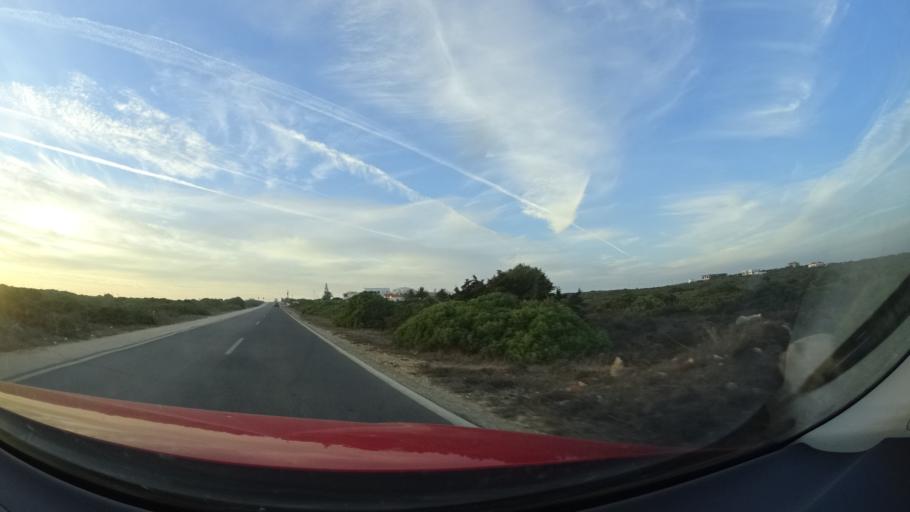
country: PT
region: Faro
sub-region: Vila do Bispo
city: Sagres
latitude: 37.0242
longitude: -8.9615
